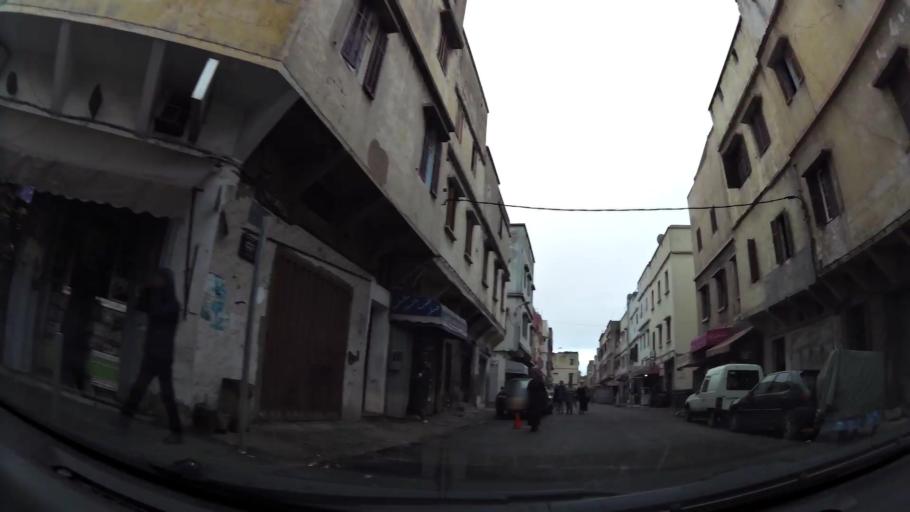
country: MA
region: Grand Casablanca
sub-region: Casablanca
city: Casablanca
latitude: 33.5707
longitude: -7.6003
